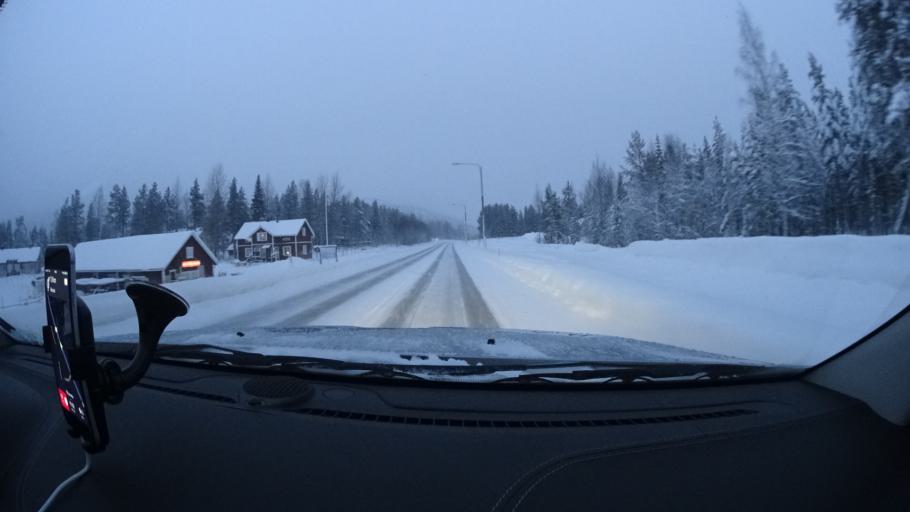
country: FI
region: Lapland
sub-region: Tunturi-Lappi
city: Kittilae
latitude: 67.7898
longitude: 24.8013
